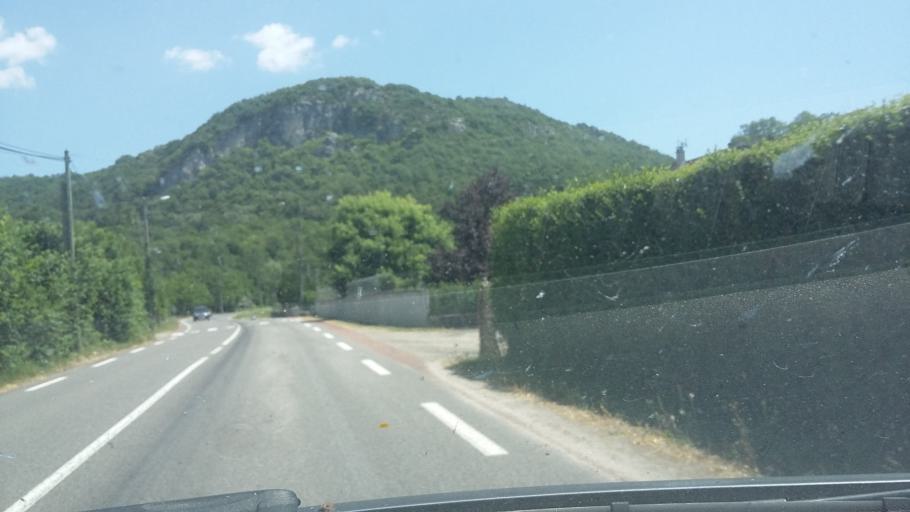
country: FR
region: Rhone-Alpes
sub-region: Departement de l'Ain
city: Virieu-le-Grand
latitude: 45.8204
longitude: 5.6507
